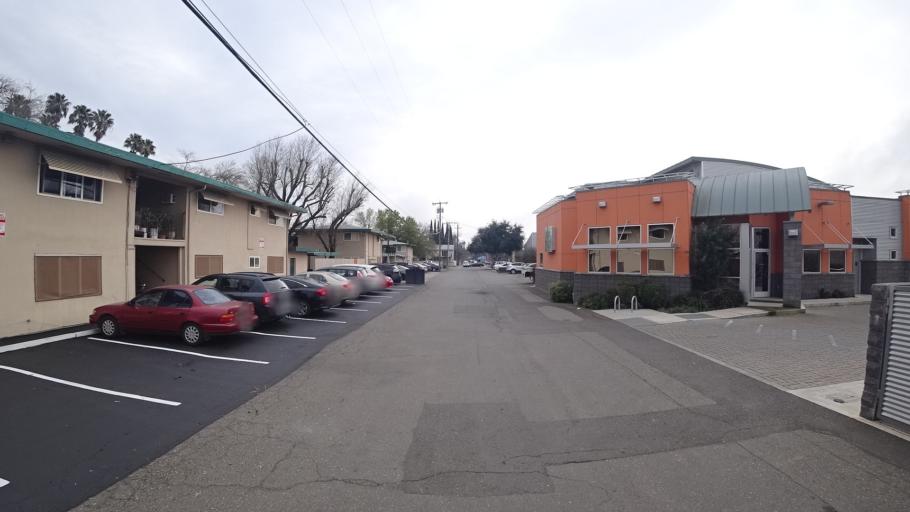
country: US
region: California
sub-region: Yolo County
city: Davis
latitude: 38.5486
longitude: -121.7386
